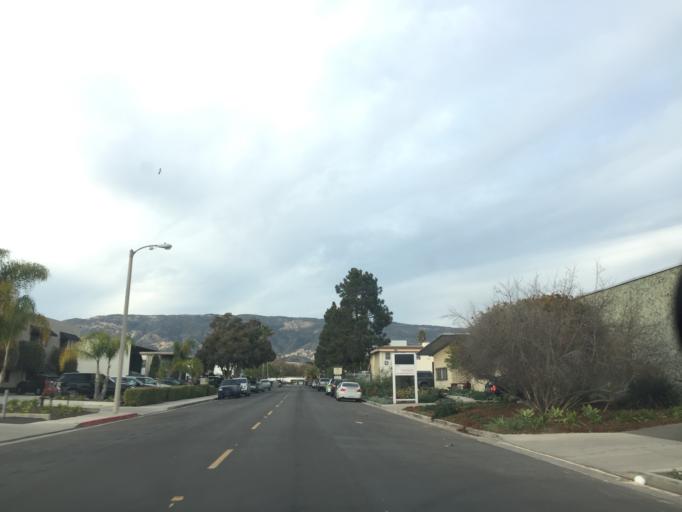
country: US
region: California
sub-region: Santa Barbara County
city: Goleta
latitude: 34.4345
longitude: -119.8485
